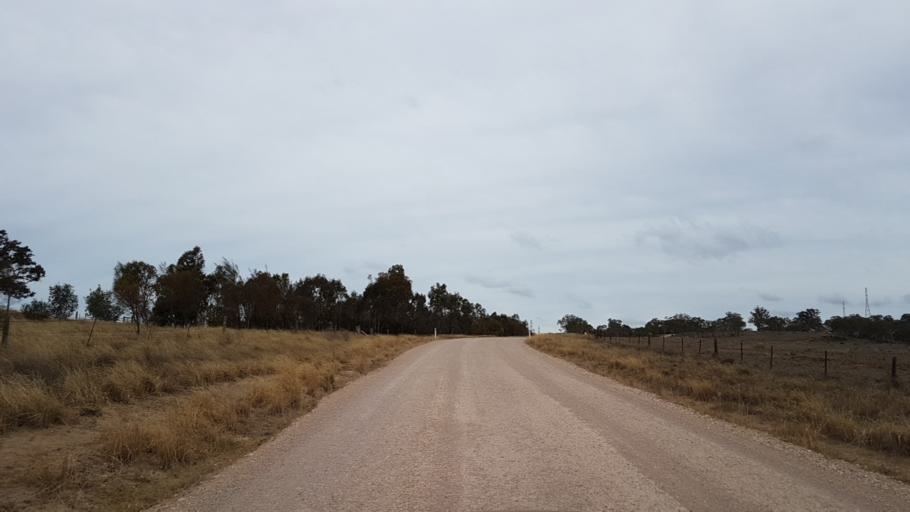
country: AU
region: South Australia
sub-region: Adelaide Hills
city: Birdwood
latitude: -34.8809
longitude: 139.0815
